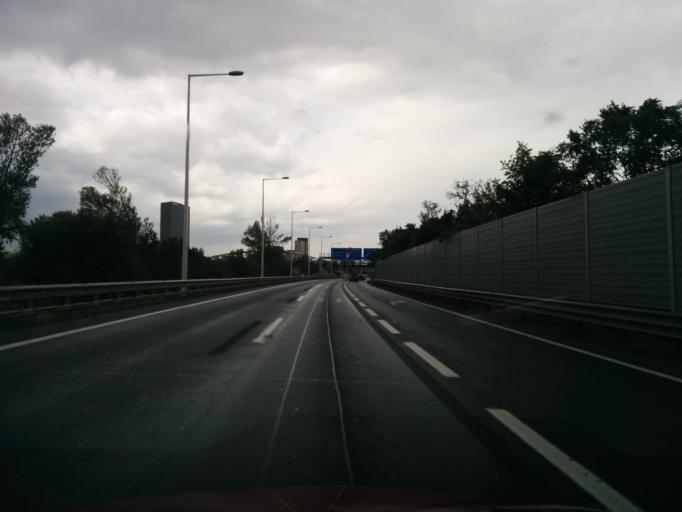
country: AT
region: Vienna
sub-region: Wien Stadt
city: Vienna
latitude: 48.1899
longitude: 16.4231
